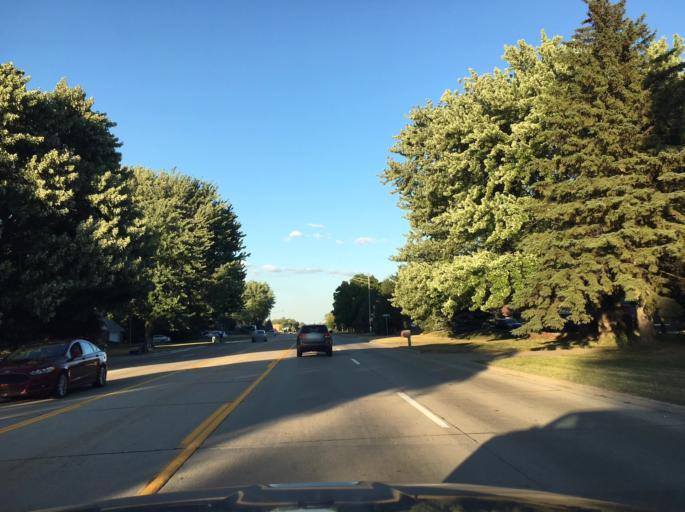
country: US
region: Michigan
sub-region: Macomb County
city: Fraser
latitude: 42.5534
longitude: -82.9577
